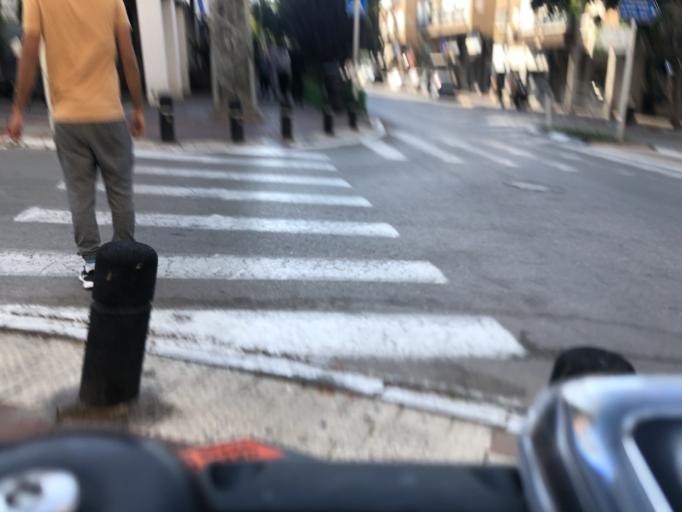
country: IL
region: Tel Aviv
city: Giv`atayim
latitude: 32.0738
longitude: 34.8086
